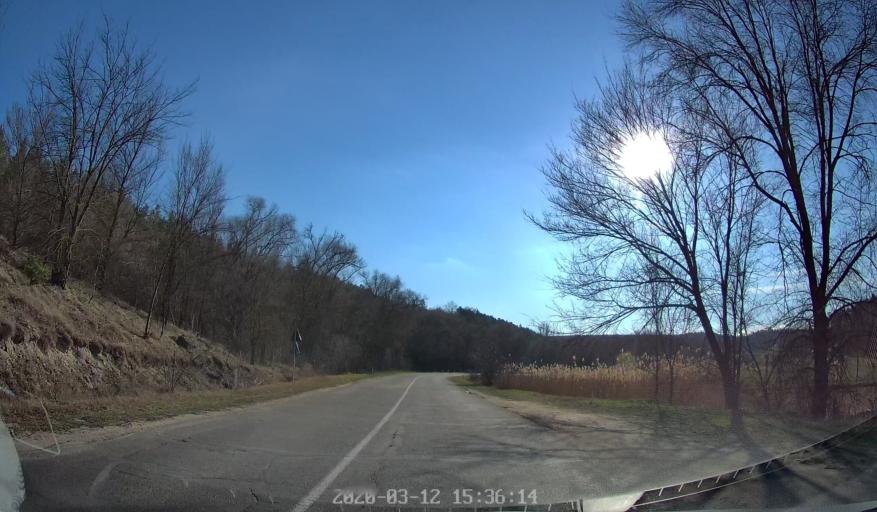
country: MD
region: Chisinau
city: Ciorescu
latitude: 47.1327
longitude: 28.9266
